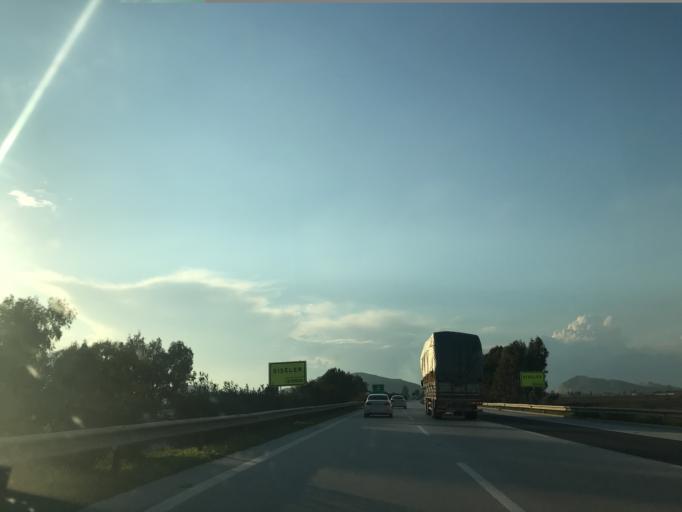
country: TR
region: Adana
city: Ceyhan
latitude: 36.9833
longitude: 35.7744
